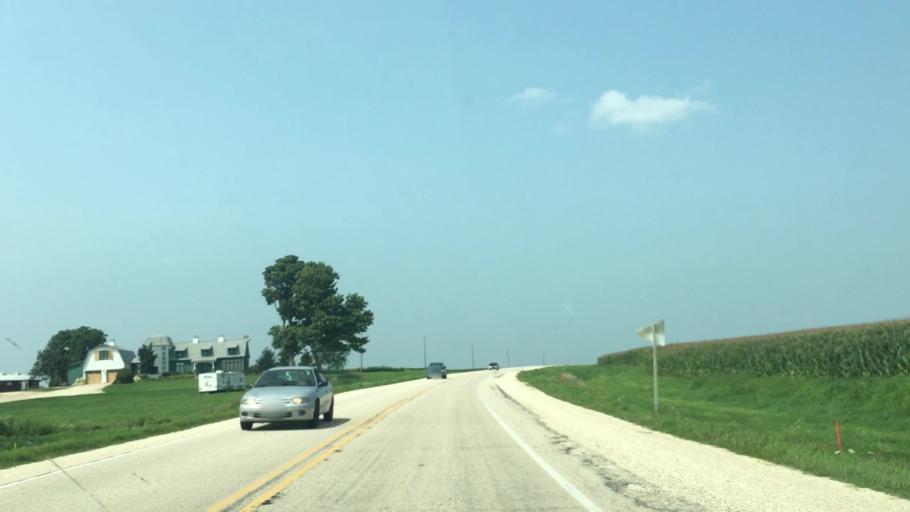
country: US
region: Iowa
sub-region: Fayette County
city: West Union
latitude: 42.9802
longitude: -91.8239
